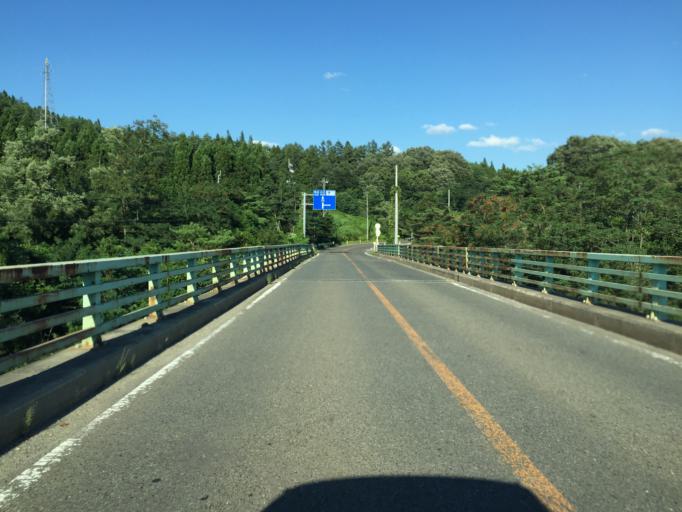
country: JP
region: Miyagi
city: Shiroishi
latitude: 37.9867
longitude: 140.4563
